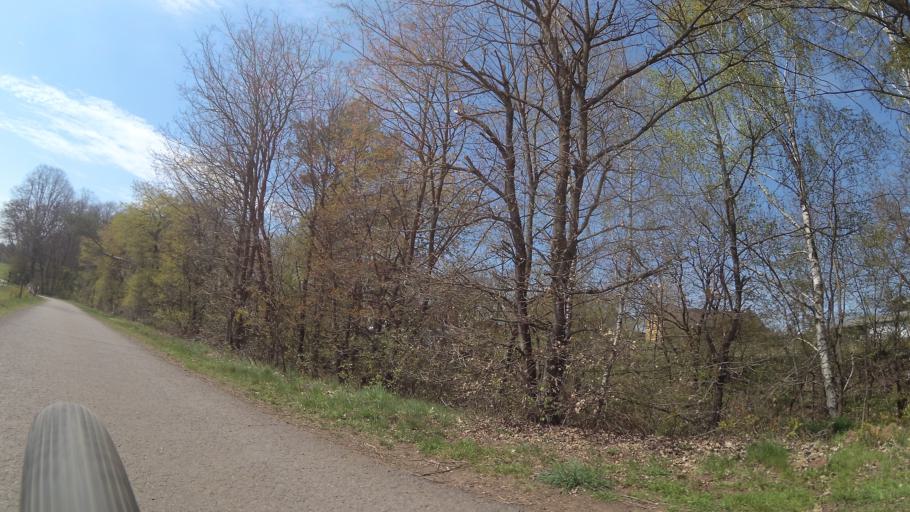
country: DE
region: Rheinland-Pfalz
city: Schonenberg-Kubelberg
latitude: 49.3996
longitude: 7.3628
